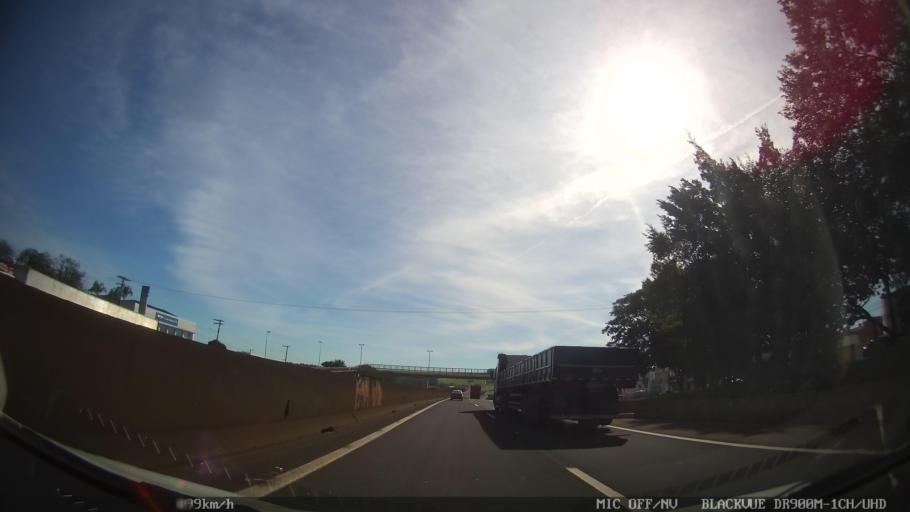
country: BR
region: Sao Paulo
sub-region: Araras
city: Araras
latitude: -22.3549
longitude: -47.3948
